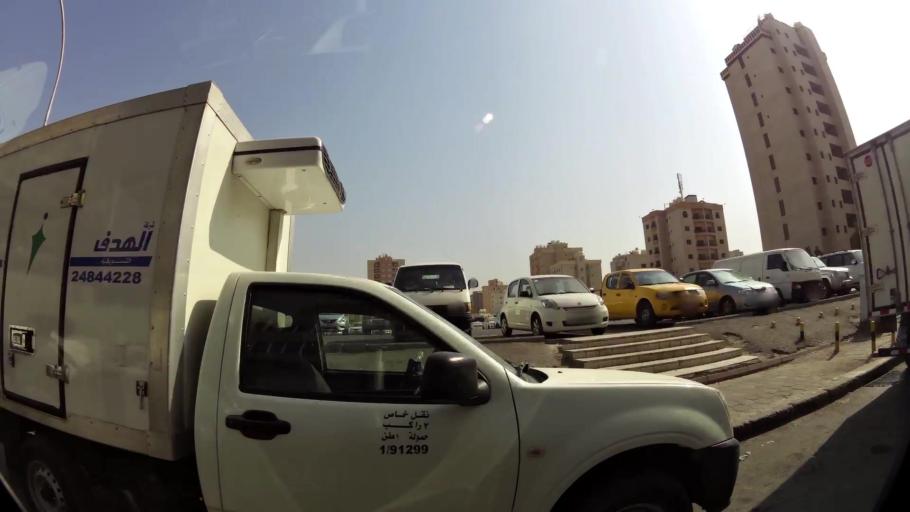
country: KW
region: Muhafazat Hawalli
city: Hawalli
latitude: 29.3284
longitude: 48.0199
